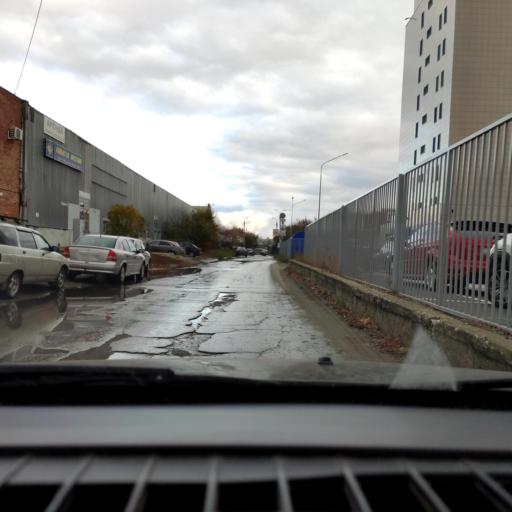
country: RU
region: Samara
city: Tol'yatti
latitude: 53.5588
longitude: 49.2957
